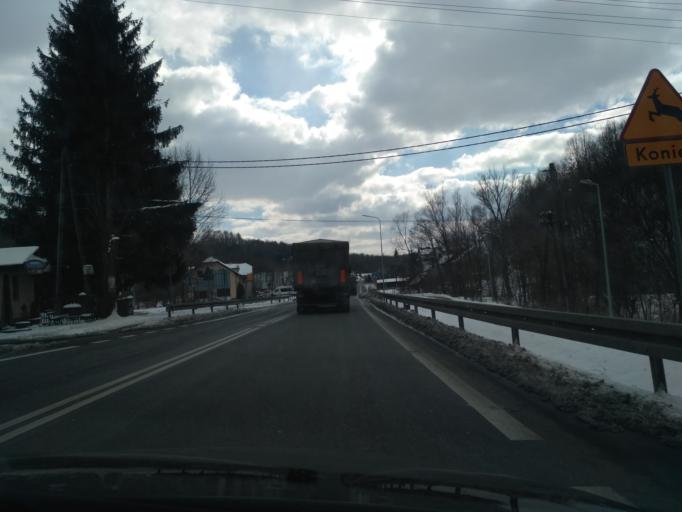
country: PL
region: Subcarpathian Voivodeship
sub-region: Powiat strzyzowski
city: Babica
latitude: 49.9210
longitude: 21.8798
